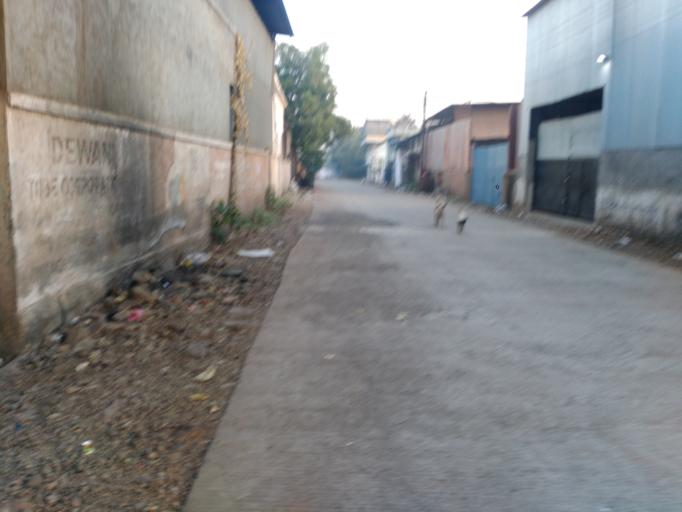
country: IN
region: Maharashtra
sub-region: Pune Division
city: Pune
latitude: 18.4522
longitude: 73.8984
